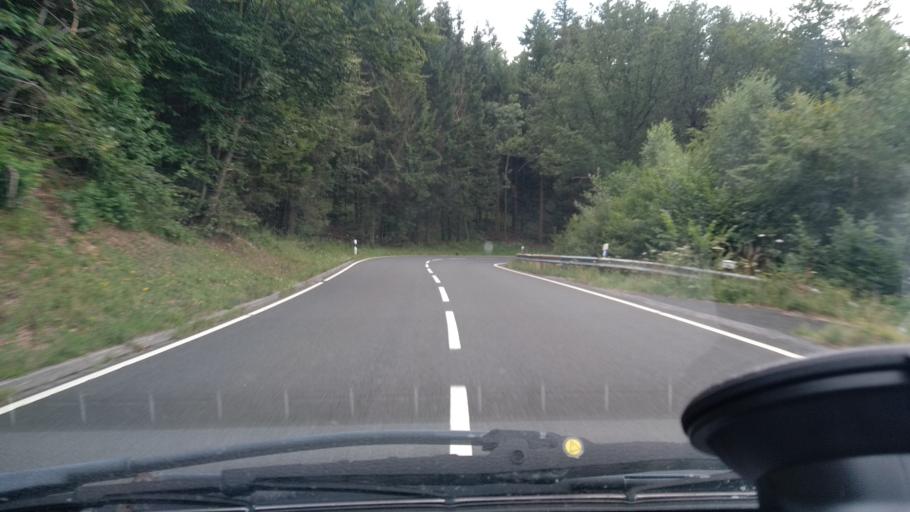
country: DE
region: Hesse
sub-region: Regierungsbezirk Giessen
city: Haiger
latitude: 50.8500
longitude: 8.2247
